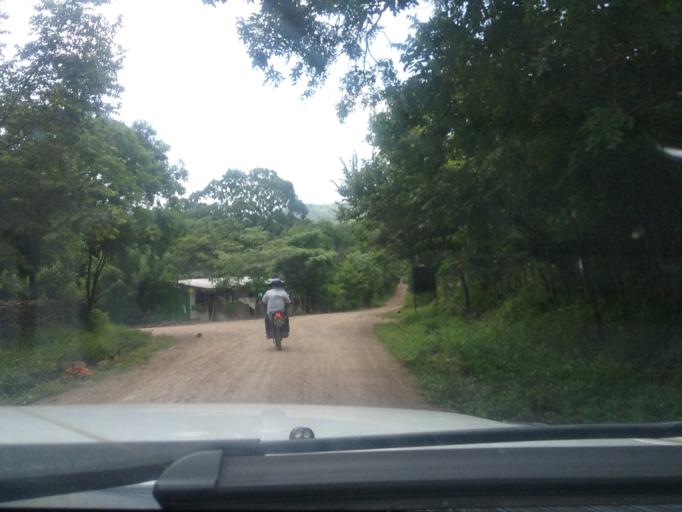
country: NI
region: Matagalpa
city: Terrabona
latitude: 12.7063
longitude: -85.9527
